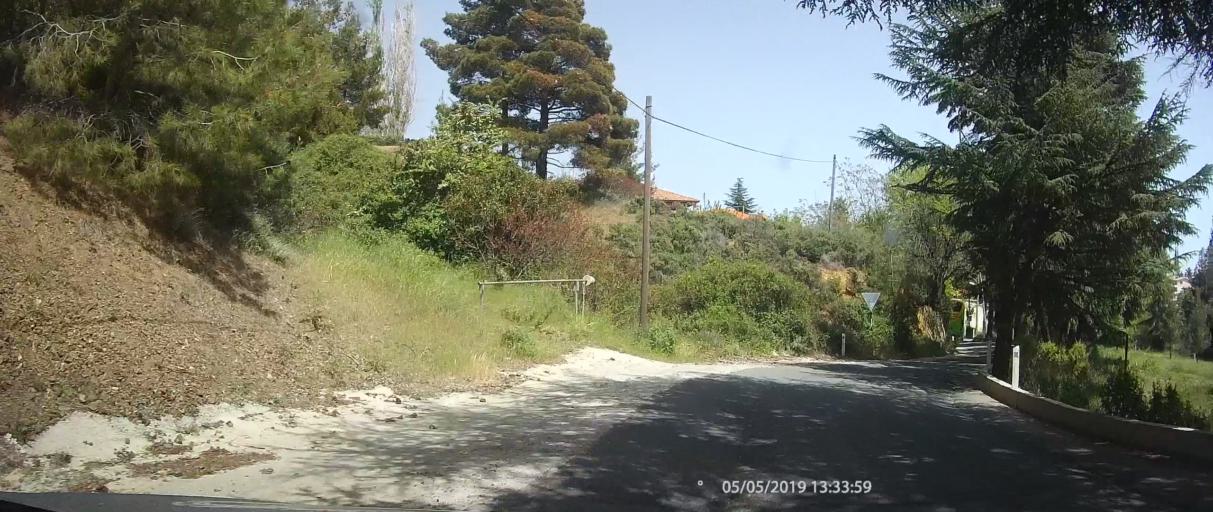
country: CY
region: Limassol
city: Pelendri
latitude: 34.8843
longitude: 32.8586
